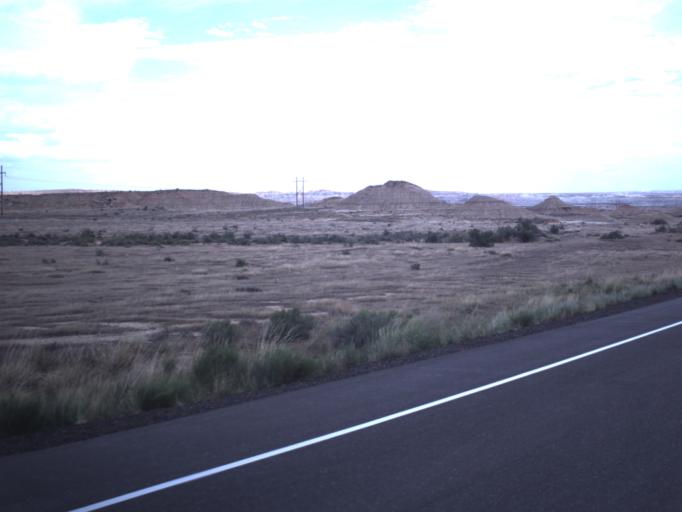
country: US
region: Utah
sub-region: Uintah County
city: Naples
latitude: 40.1218
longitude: -109.2571
